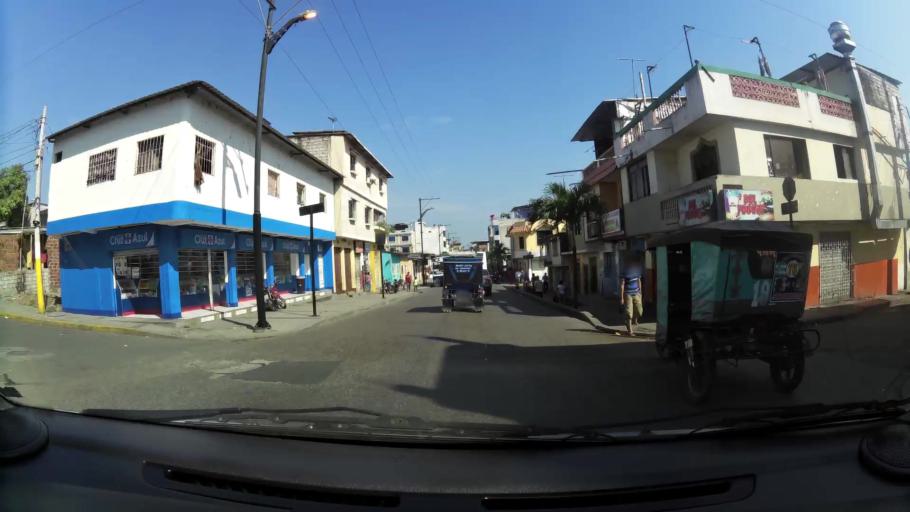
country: EC
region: Guayas
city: Eloy Alfaro
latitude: -2.1006
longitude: -79.9275
